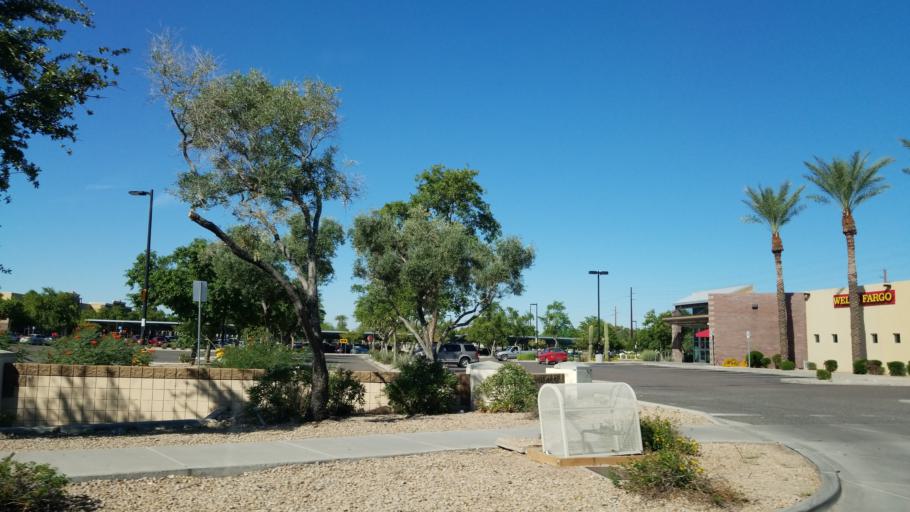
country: US
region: Arizona
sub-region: Maricopa County
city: Glendale
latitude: 33.5523
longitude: -112.1776
